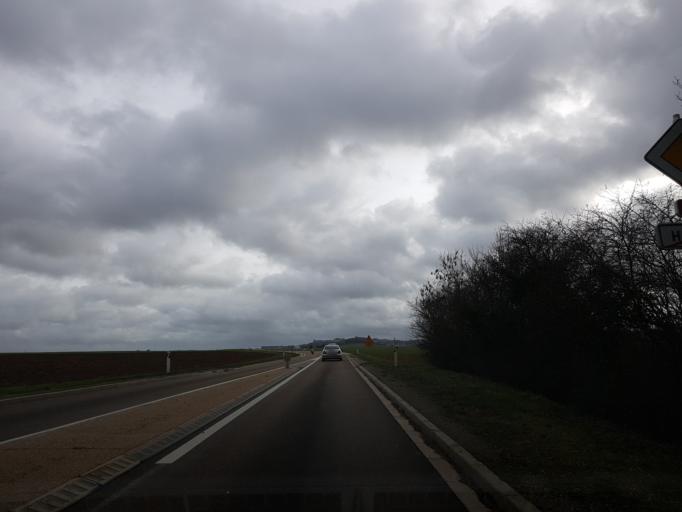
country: FR
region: Champagne-Ardenne
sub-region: Departement de la Haute-Marne
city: Langres
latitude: 47.8999
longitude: 5.3074
